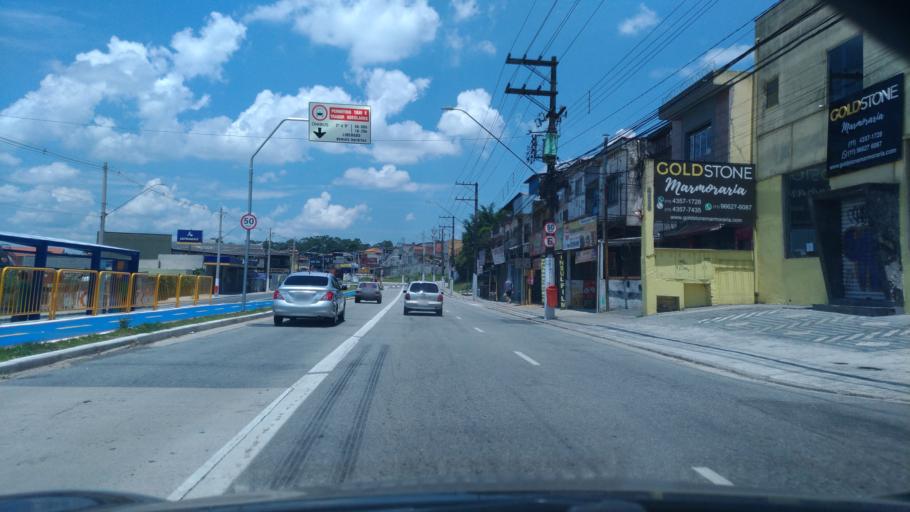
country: BR
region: Sao Paulo
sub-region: Sao Bernardo Do Campo
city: Sao Bernardo do Campo
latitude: -23.7357
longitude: -46.5885
